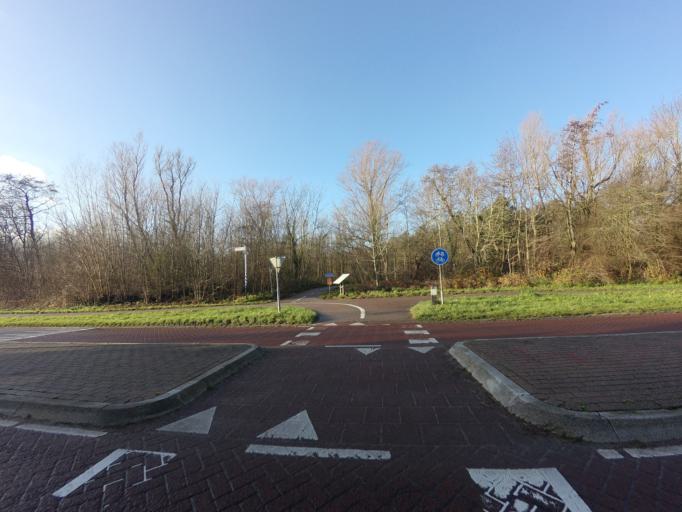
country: NL
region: North Holland
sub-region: Gemeente Texel
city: Den Burg
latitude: 53.1513
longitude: 4.8656
